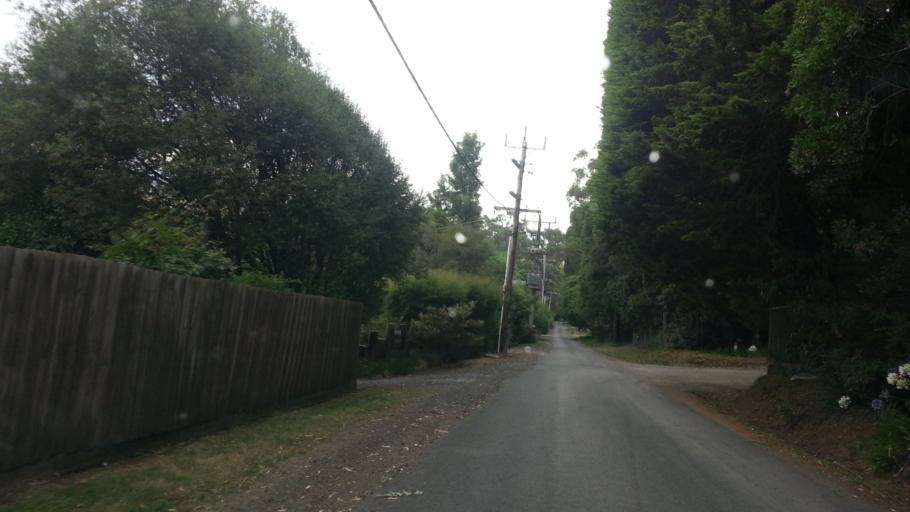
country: AU
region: Victoria
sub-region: Cardinia
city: Emerald
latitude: -37.9257
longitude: 145.4279
